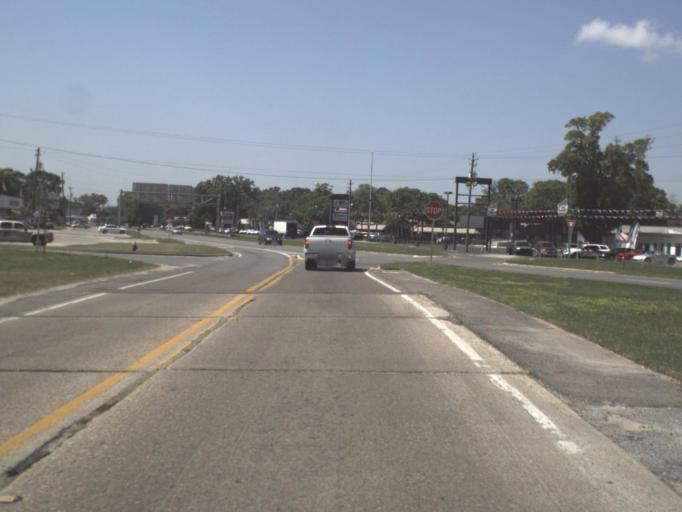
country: US
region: Florida
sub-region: Escambia County
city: West Pensacola
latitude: 30.4230
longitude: -87.2743
